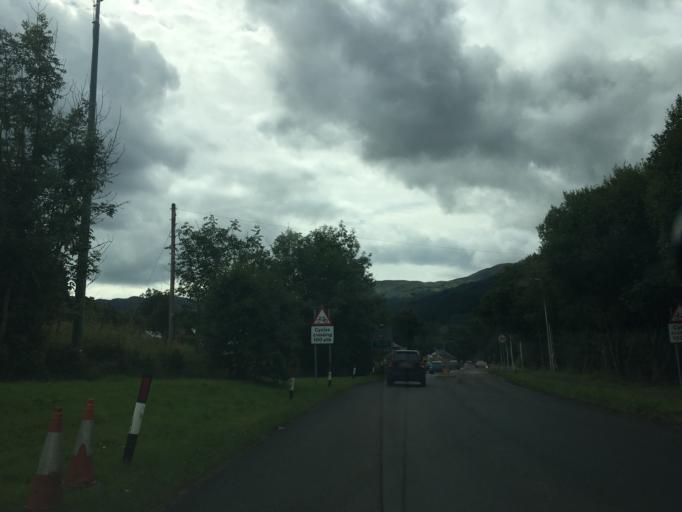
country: GB
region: Scotland
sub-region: Stirling
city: Callander
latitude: 56.3292
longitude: -4.3253
